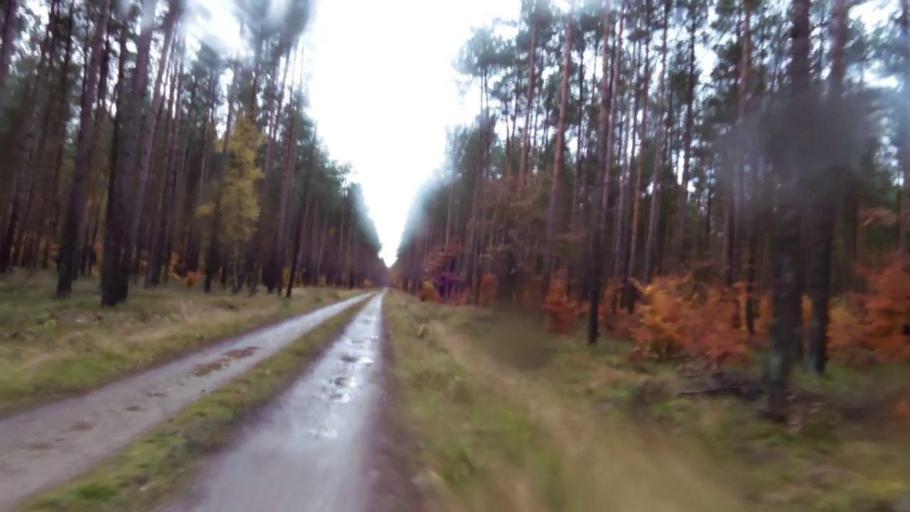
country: PL
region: West Pomeranian Voivodeship
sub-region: Powiat goleniowski
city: Stepnica
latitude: 53.6461
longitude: 14.7007
